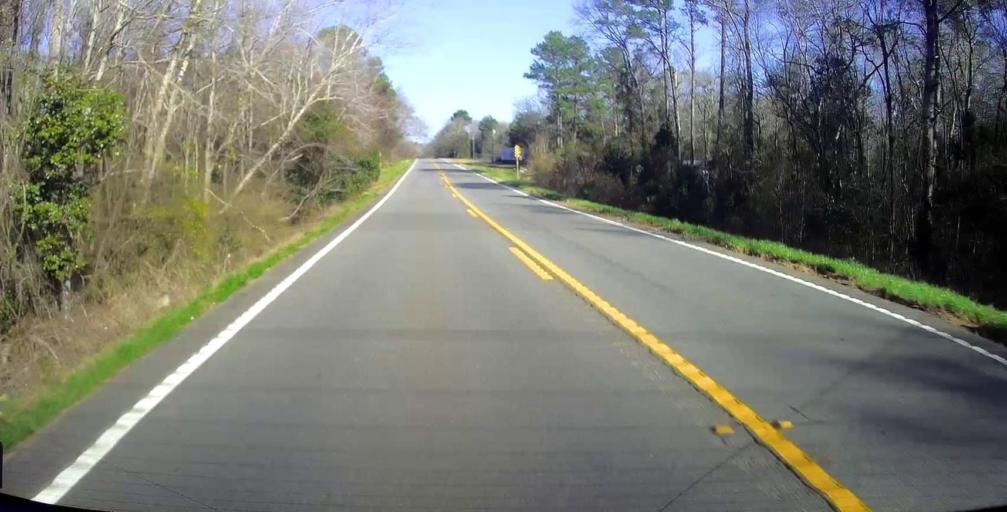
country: US
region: Georgia
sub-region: Macon County
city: Oglethorpe
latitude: 32.3516
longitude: -84.1628
